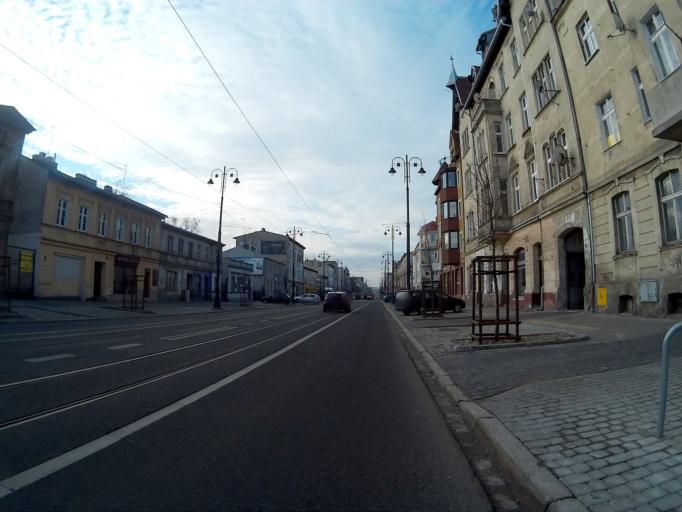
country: PL
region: Kujawsko-Pomorskie
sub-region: Bydgoszcz
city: Bydgoszcz
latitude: 53.1359
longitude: 18.0138
